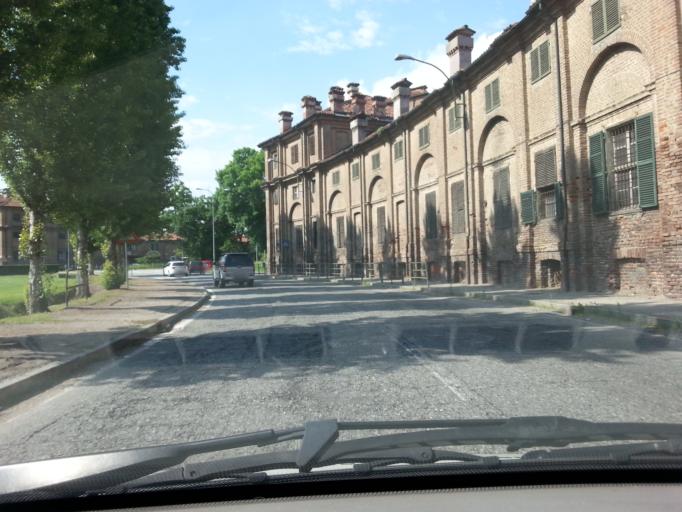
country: IT
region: Piedmont
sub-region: Provincia di Torino
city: Garino
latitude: 44.9967
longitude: 7.6073
